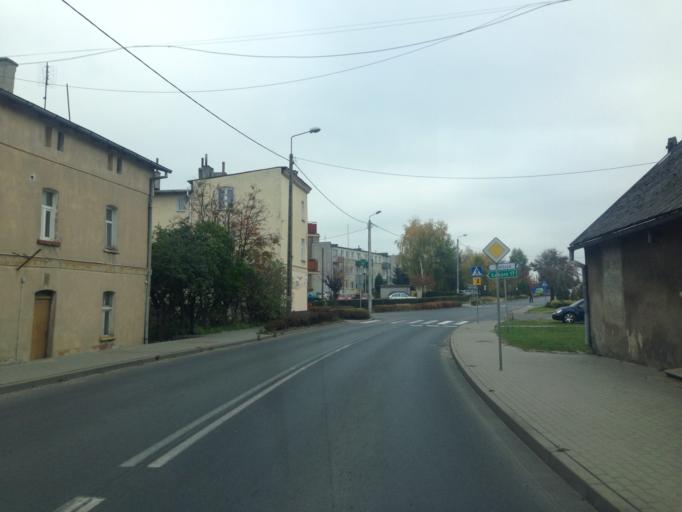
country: PL
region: Kujawsko-Pomorskie
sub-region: Powiat brodnicki
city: Jablonowo Pomorskie
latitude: 53.3876
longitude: 19.1521
